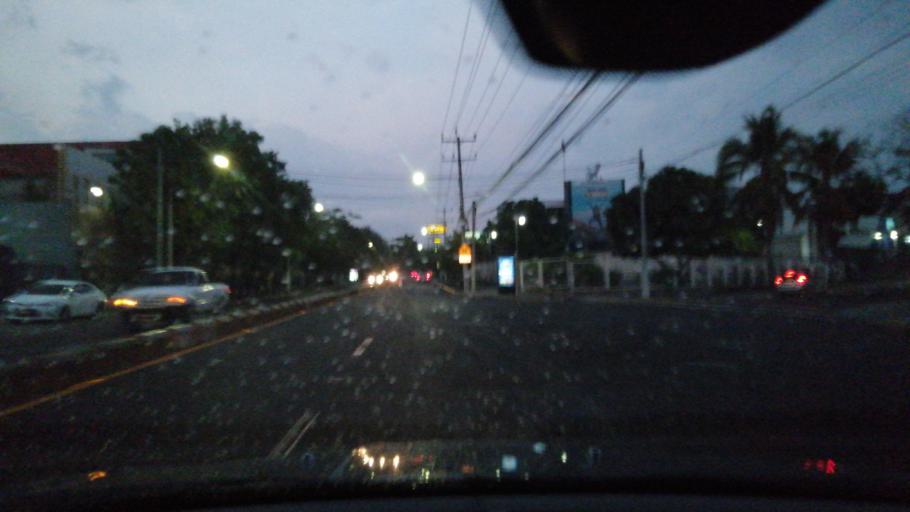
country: SV
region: San Salvador
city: San Salvador
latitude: 13.7075
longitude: -89.2041
